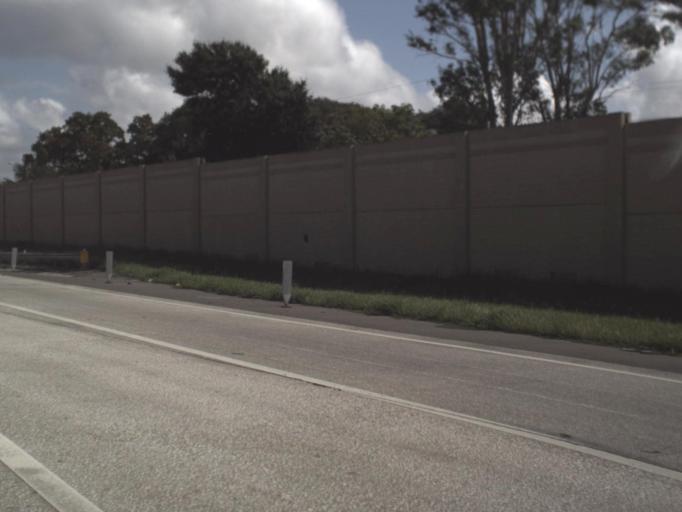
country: US
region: Florida
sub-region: Hillsborough County
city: University
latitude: 28.0498
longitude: -82.4547
